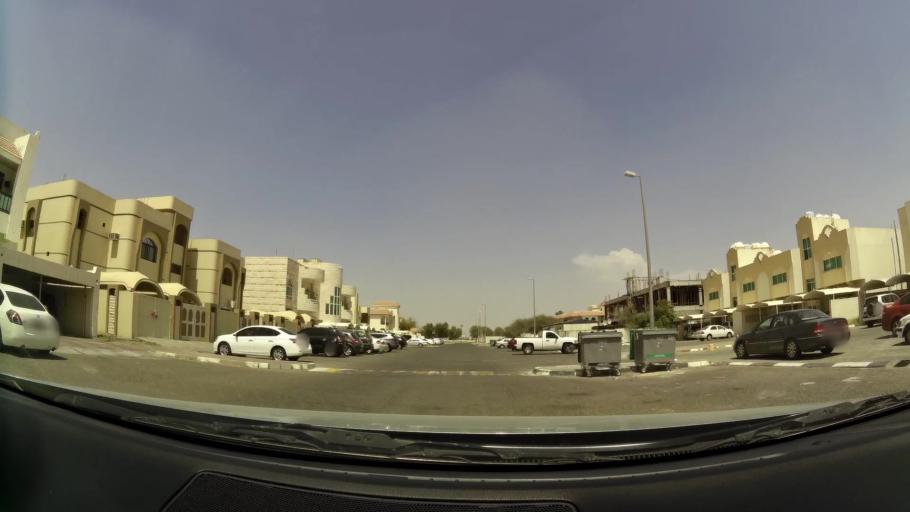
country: AE
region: Abu Dhabi
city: Al Ain
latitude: 24.2382
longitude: 55.7168
